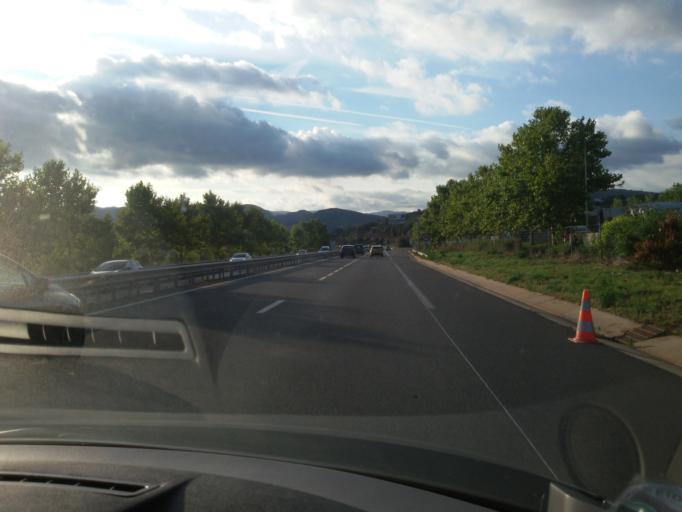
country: FR
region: Languedoc-Roussillon
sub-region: Departement de l'Herault
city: Lodeve
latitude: 43.6893
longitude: 3.3525
